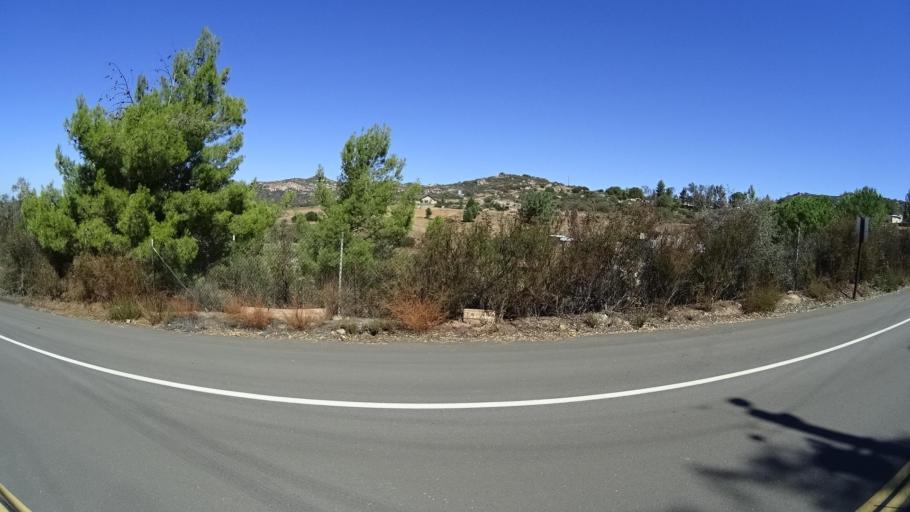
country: US
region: California
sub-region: San Diego County
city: Descanso
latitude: 32.7643
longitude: -116.6776
